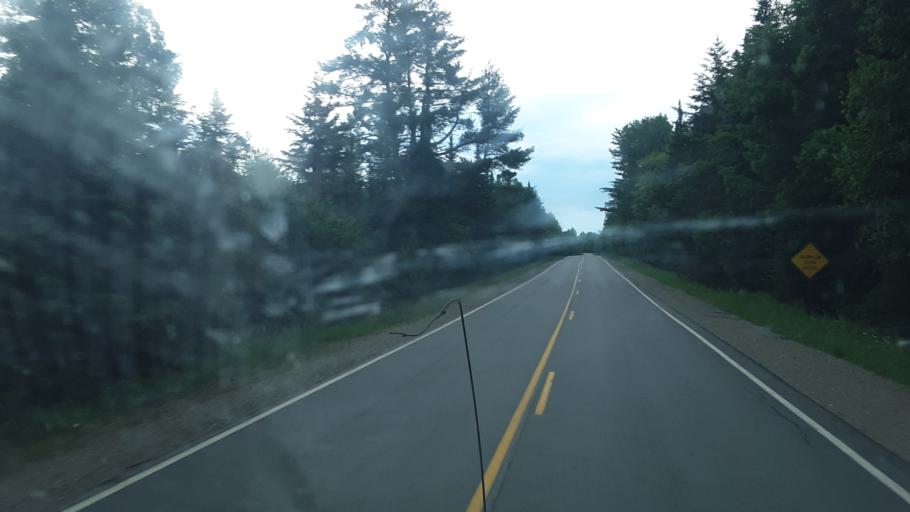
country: US
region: Maine
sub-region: Penobscot County
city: Medway
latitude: 45.6779
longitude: -68.2793
